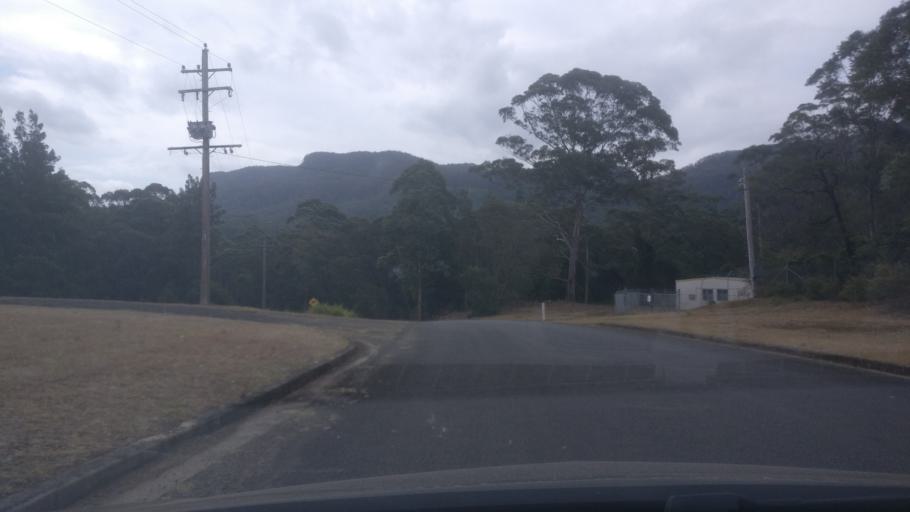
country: AU
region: New South Wales
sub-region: Shoalhaven Shire
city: Kangaroo Valley
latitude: -34.7231
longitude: 150.4783
